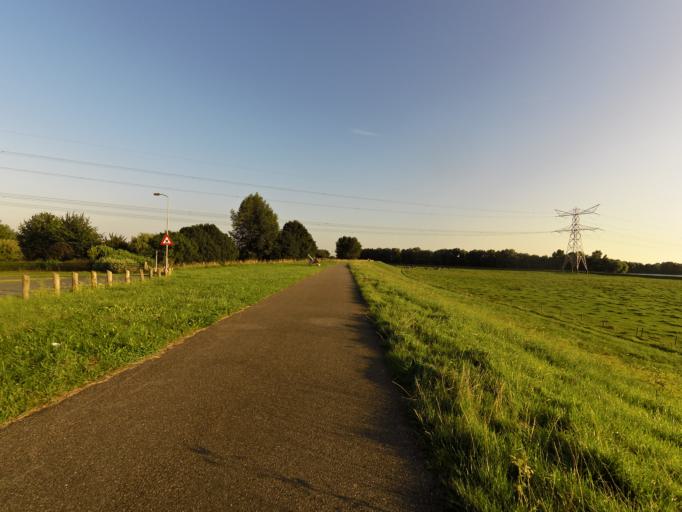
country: NL
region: Gelderland
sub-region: Gemeente Duiven
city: Duiven
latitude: 51.9227
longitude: 5.9922
